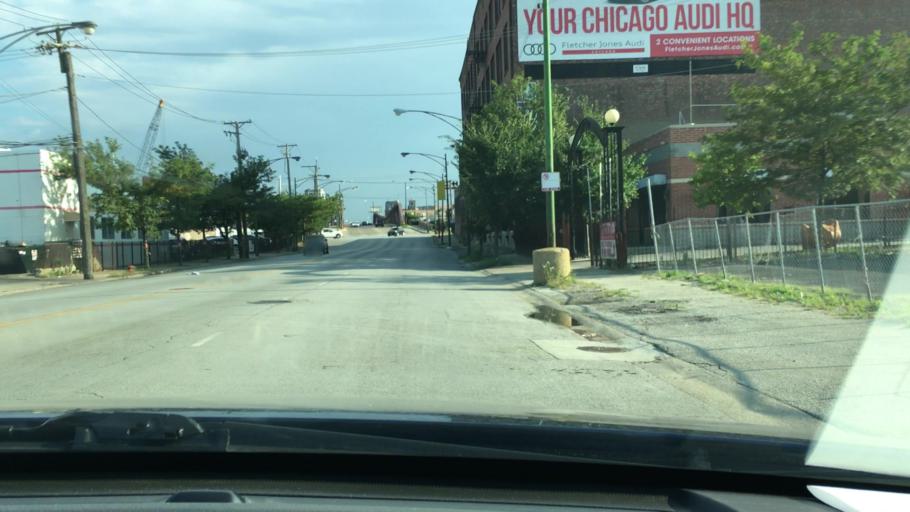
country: US
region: Illinois
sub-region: Cook County
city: Chicago
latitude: 41.8572
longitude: -87.6390
